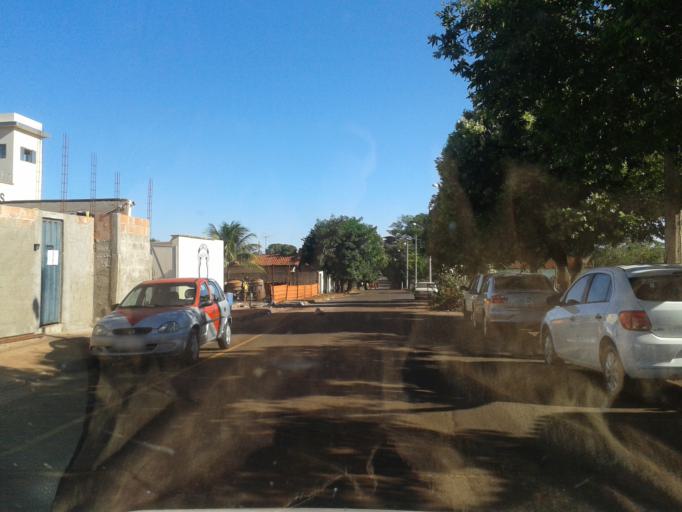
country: BR
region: Minas Gerais
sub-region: Centralina
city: Centralina
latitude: -18.7215
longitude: -49.2055
